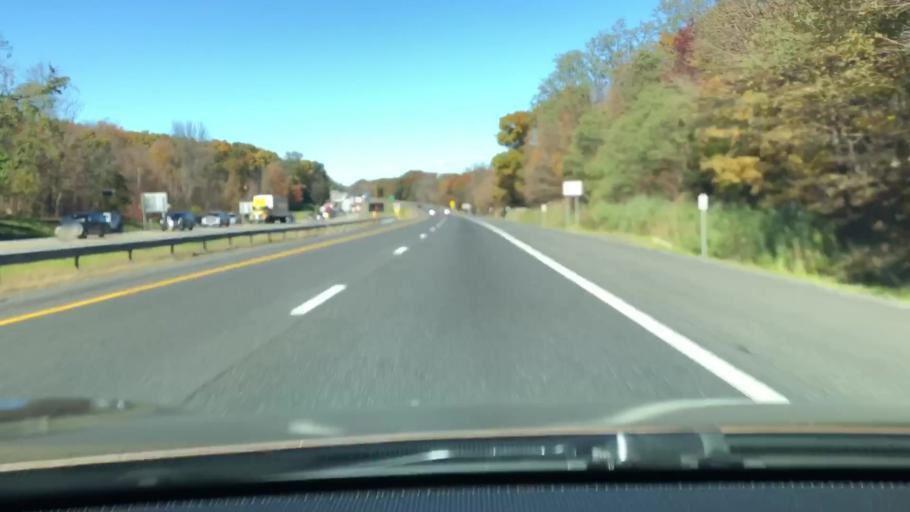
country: US
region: New York
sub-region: Orange County
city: Gardnertown
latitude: 41.5348
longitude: -74.0759
